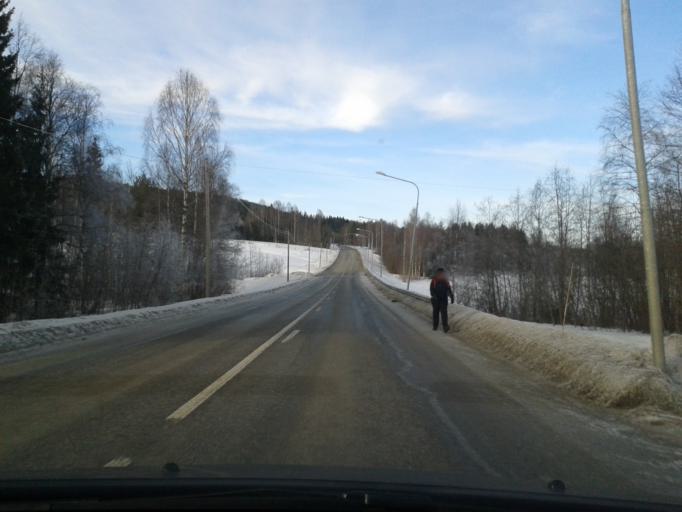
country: SE
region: Vaesternorrland
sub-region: OErnskoeldsviks Kommun
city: Bredbyn
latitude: 63.4860
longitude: 18.0862
